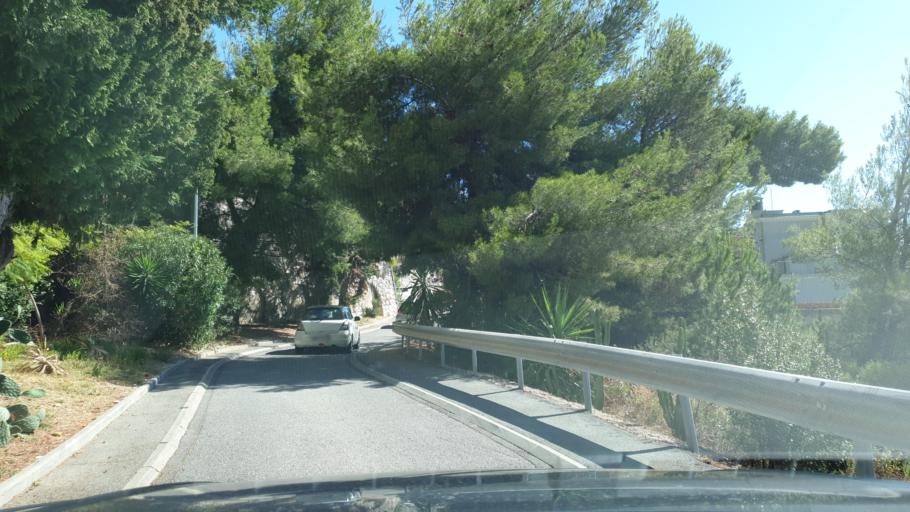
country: FR
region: Provence-Alpes-Cote d'Azur
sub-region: Departement des Alpes-Maritimes
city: Eze
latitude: 43.7201
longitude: 7.3701
